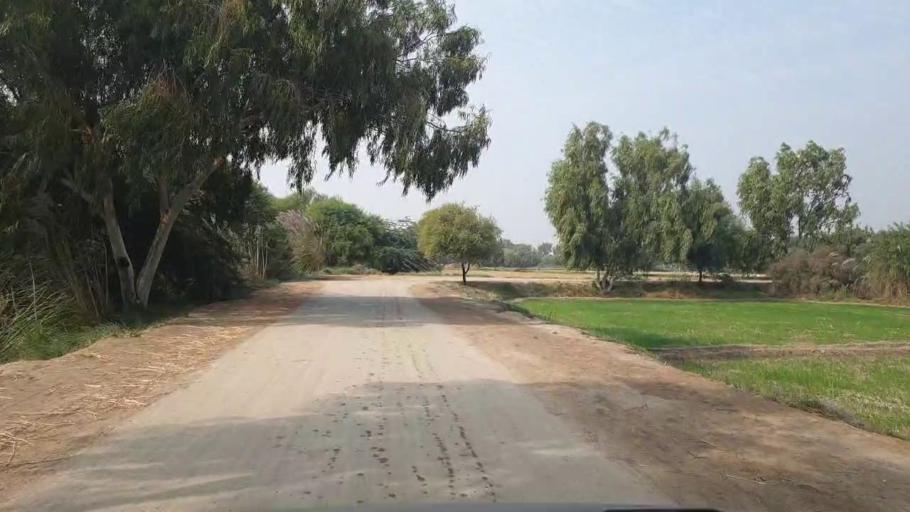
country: PK
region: Sindh
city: Tando Muhammad Khan
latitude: 25.1209
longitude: 68.4604
